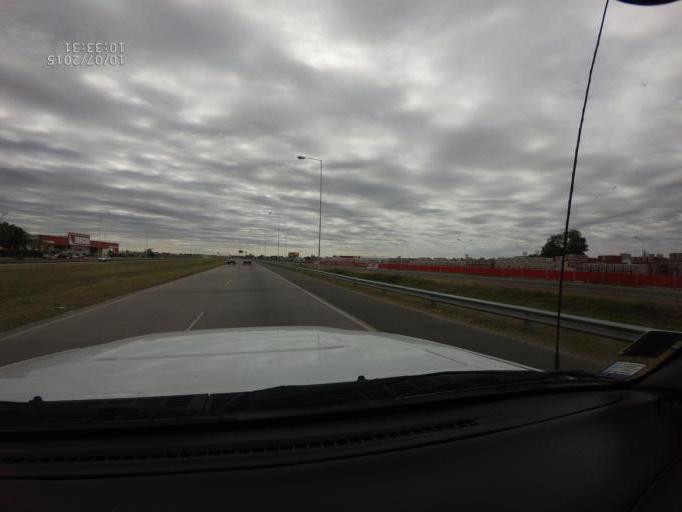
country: AR
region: Cordoba
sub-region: Departamento de Capital
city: Cordoba
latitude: -31.3551
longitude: -64.2115
